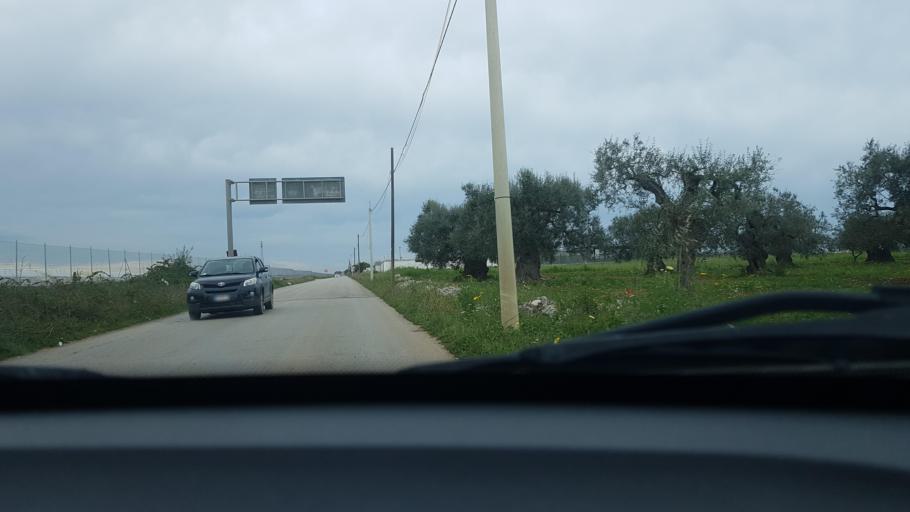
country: IT
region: Apulia
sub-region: Provincia di Bari
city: Noicattaro
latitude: 41.0341
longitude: 16.9763
